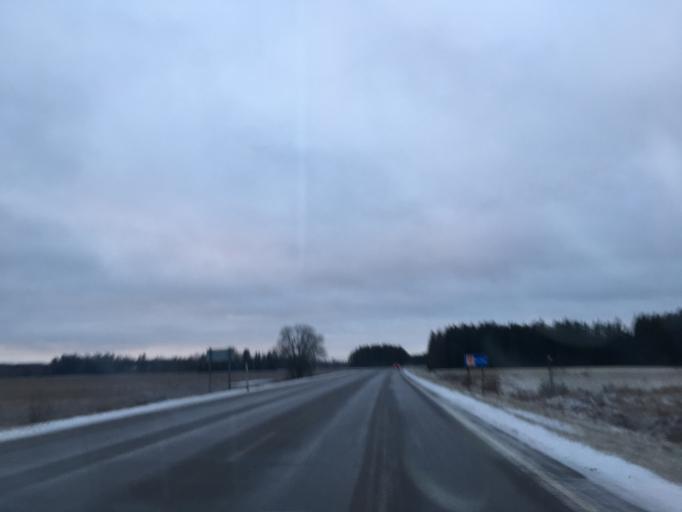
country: FI
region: Varsinais-Suomi
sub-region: Loimaa
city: Aura
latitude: 60.6619
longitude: 22.5599
